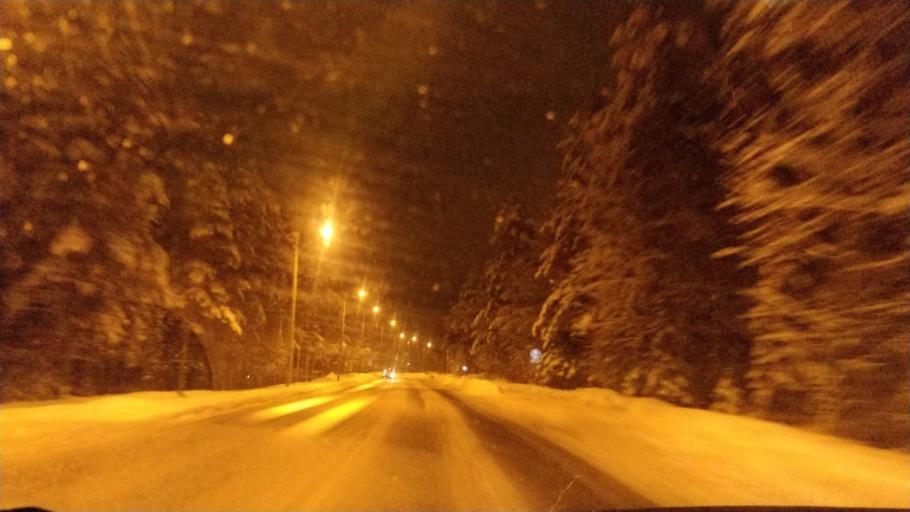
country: FI
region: Lapland
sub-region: Rovaniemi
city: Rovaniemi
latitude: 66.3786
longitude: 25.3809
